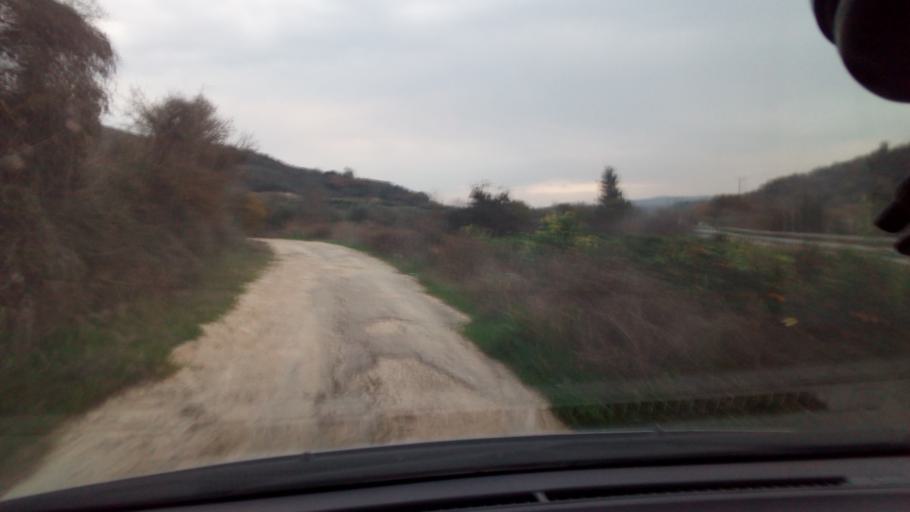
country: CY
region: Pafos
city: Polis
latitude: 34.9521
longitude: 32.4679
